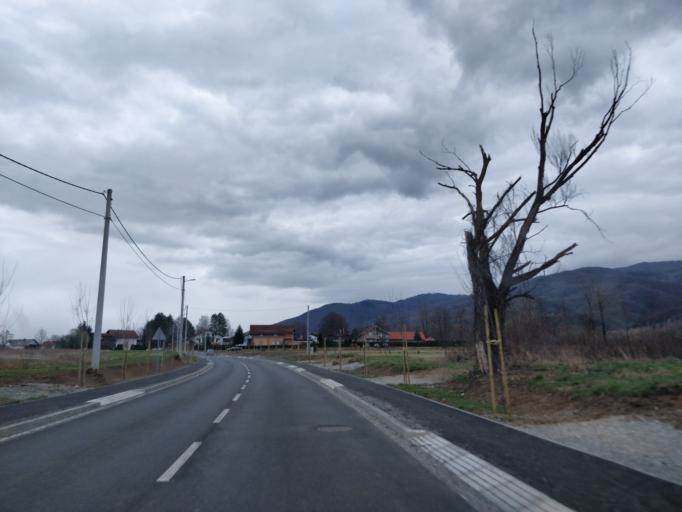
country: HR
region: Zagrebacka
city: Jablanovec
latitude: 45.8992
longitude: 15.8632
